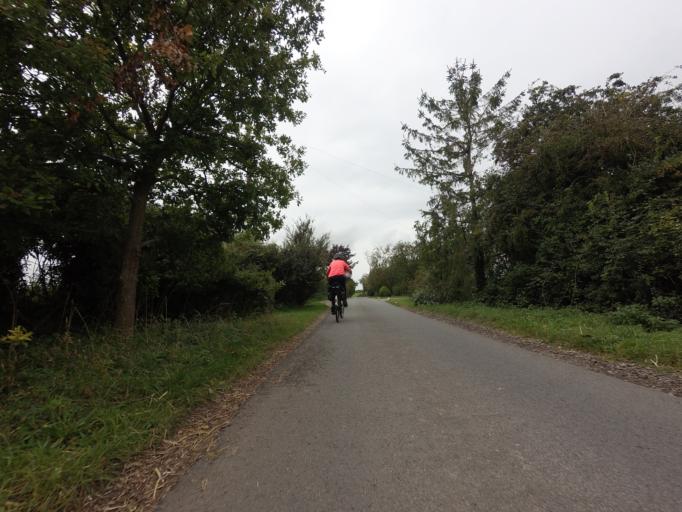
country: GB
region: England
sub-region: Cambridgeshire
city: Duxford
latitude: 52.0469
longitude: 0.1454
